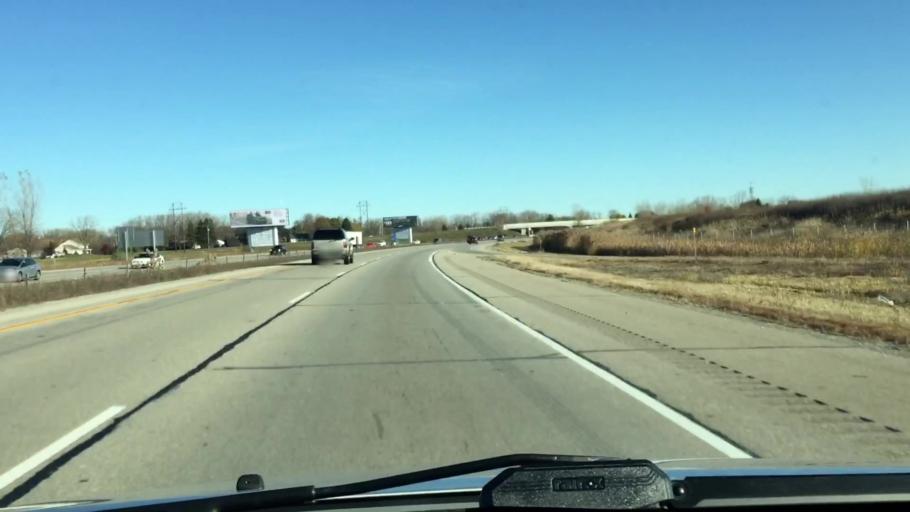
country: US
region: Wisconsin
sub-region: Outagamie County
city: Appleton
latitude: 44.2907
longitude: -88.4658
